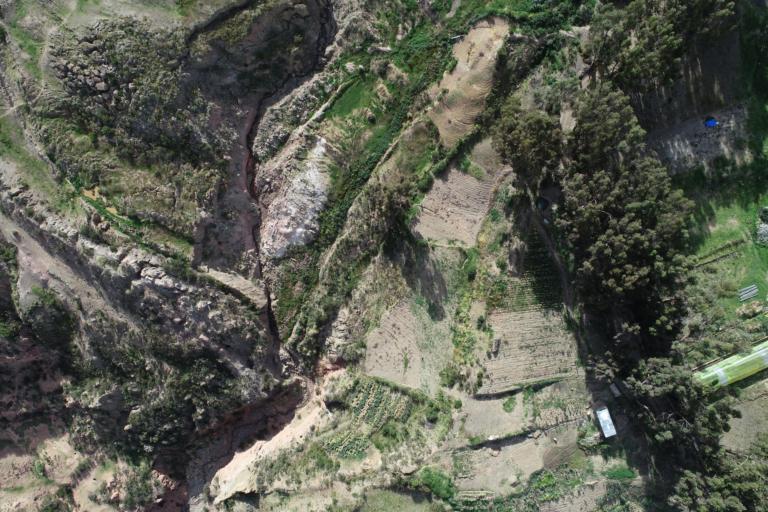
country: BO
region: La Paz
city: La Paz
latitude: -16.5510
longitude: -67.9937
